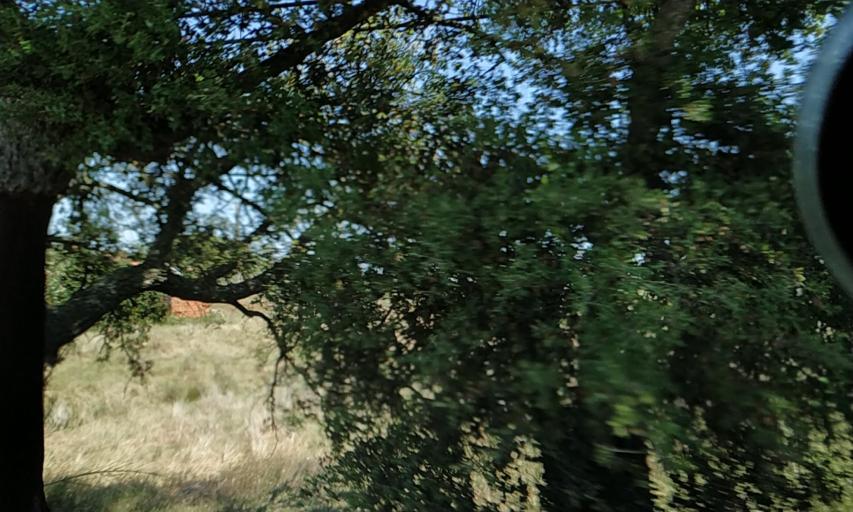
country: PT
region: Setubal
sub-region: Palmela
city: Pinhal Novo
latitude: 38.6614
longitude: -8.7390
